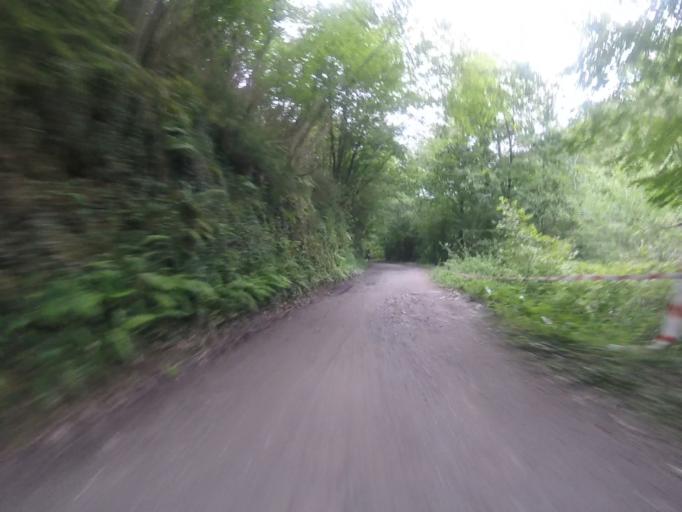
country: ES
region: Navarre
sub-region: Provincia de Navarra
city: Etxalar
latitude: 43.2091
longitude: -1.6653
